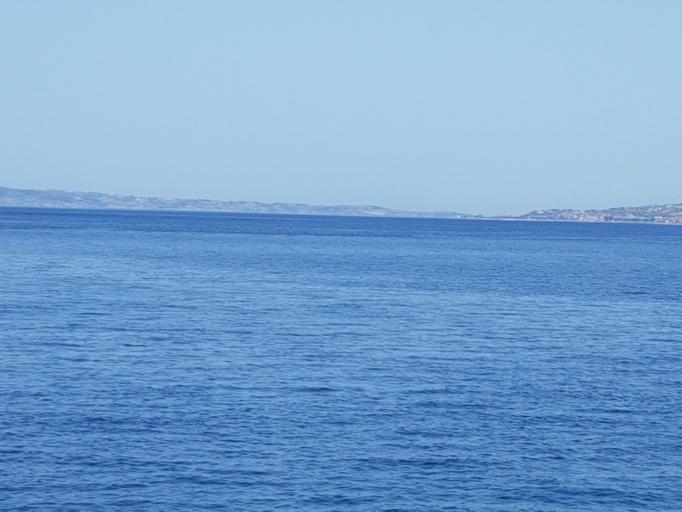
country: IT
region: Calabria
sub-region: Provincia di Reggio Calabria
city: Reggio Calabria
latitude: 38.1008
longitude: 15.6425
